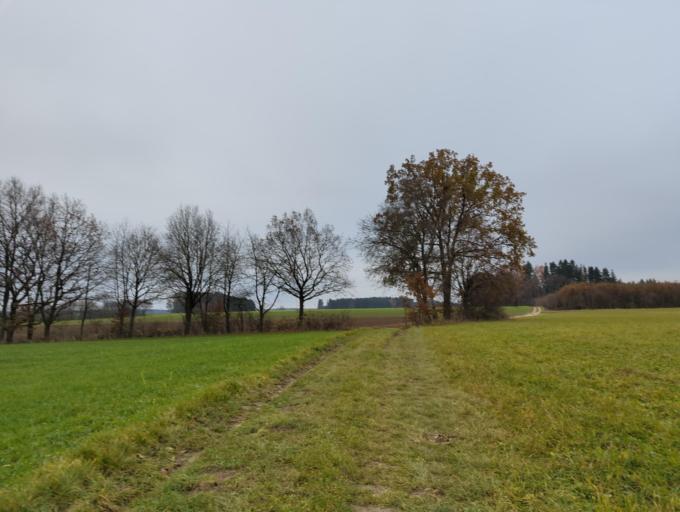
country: DE
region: Bavaria
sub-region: Swabia
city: Rettenbach
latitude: 48.4357
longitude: 10.3212
